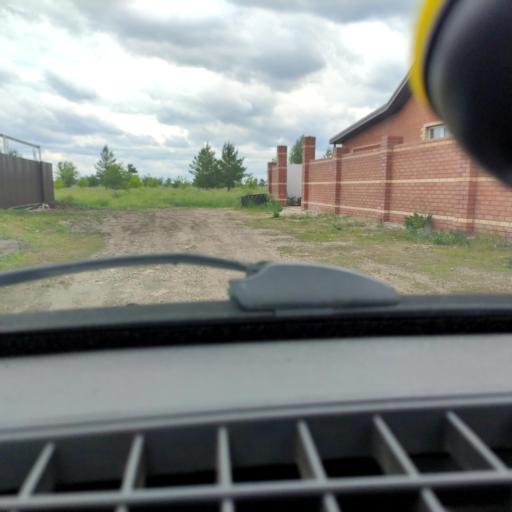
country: RU
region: Samara
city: Povolzhskiy
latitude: 53.5982
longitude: 49.5830
